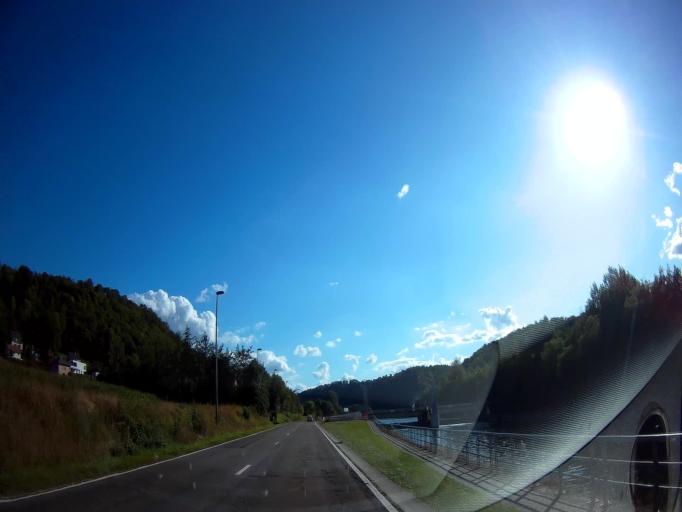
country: BE
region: Wallonia
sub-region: Province de Namur
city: Anhee
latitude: 50.2975
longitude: 4.8990
